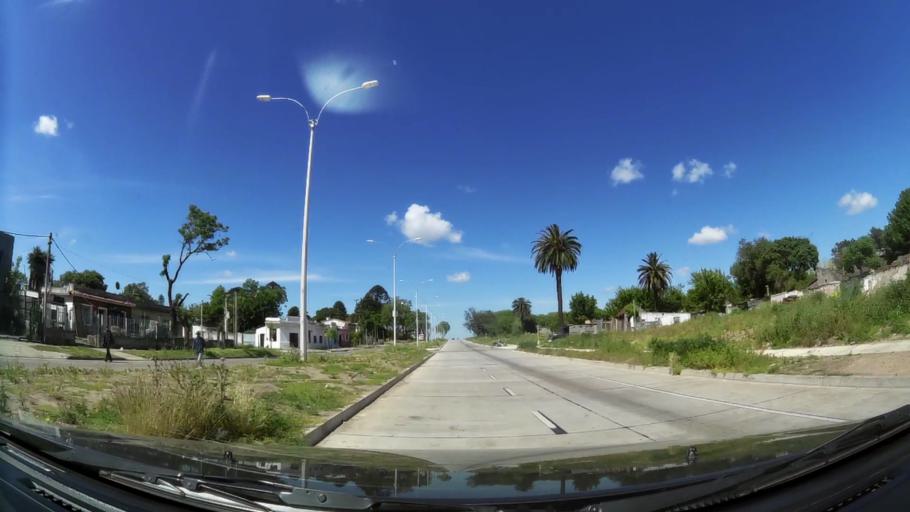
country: UY
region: Montevideo
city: Montevideo
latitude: -34.8444
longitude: -56.1441
